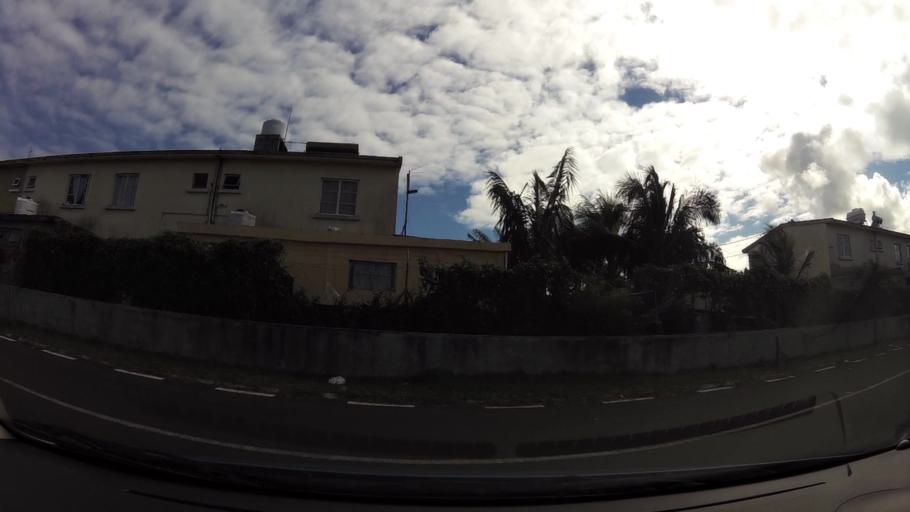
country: MU
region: Grand Port
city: Beau Vallon
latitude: -20.4209
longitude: 57.7072
